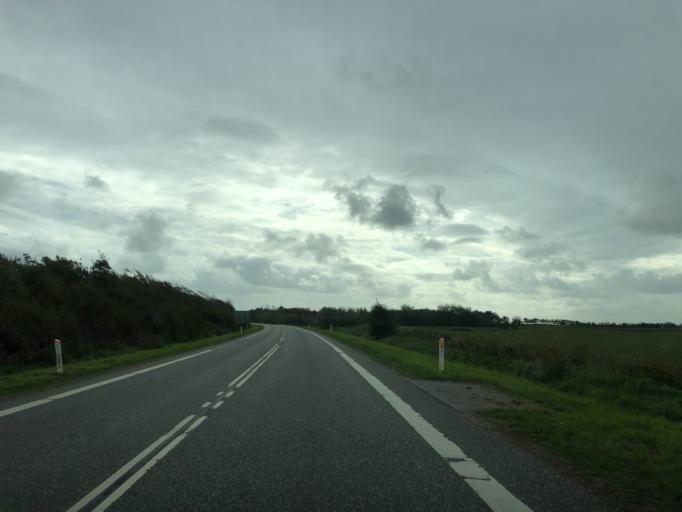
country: DK
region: North Denmark
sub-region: Thisted Kommune
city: Hurup
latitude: 56.7416
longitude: 8.4369
